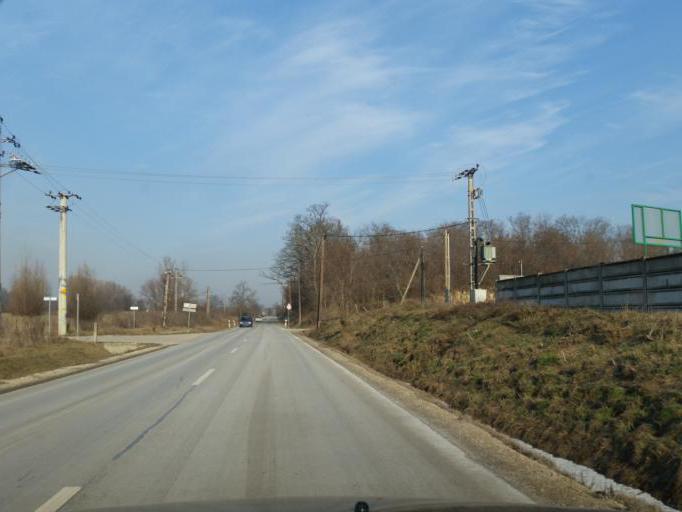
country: HU
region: Pest
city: Paty
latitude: 47.5008
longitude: 18.8254
